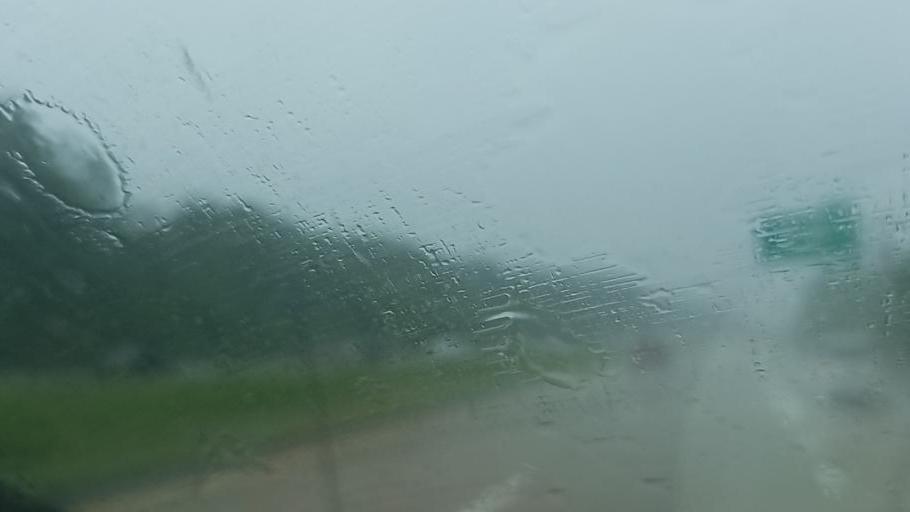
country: US
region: Delaware
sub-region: Kent County
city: Dover
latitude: 39.1995
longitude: -75.5361
